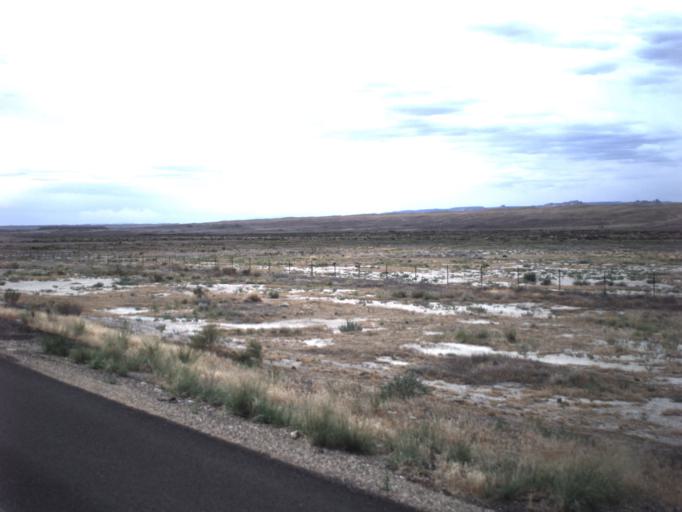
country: US
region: Utah
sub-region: Carbon County
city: East Carbon City
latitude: 39.0664
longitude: -110.3143
